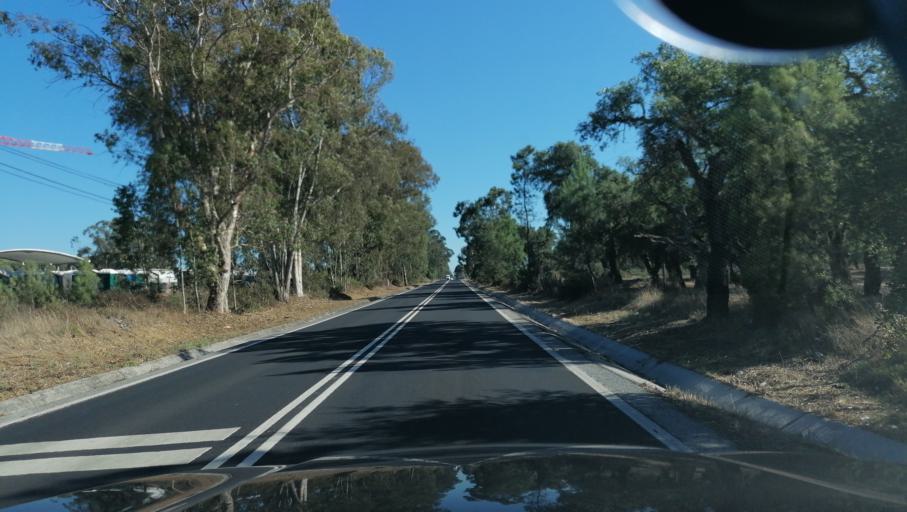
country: PT
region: Santarem
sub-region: Benavente
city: Poceirao
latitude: 38.8350
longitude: -8.8810
